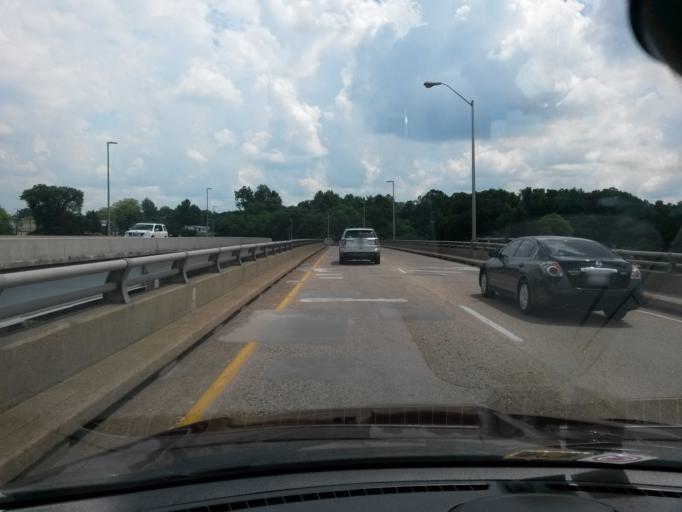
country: US
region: Virginia
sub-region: City of Hopewell
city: Hopewell
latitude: 37.3116
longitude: -77.2970
